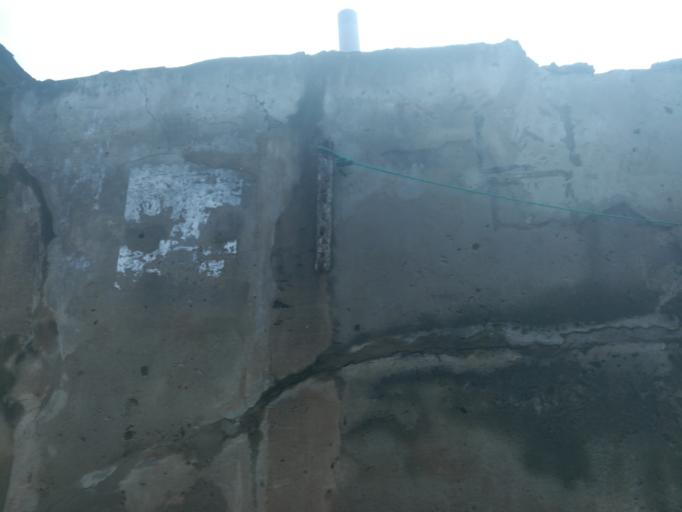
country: NG
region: Lagos
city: Agege
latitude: 6.6158
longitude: 3.3305
